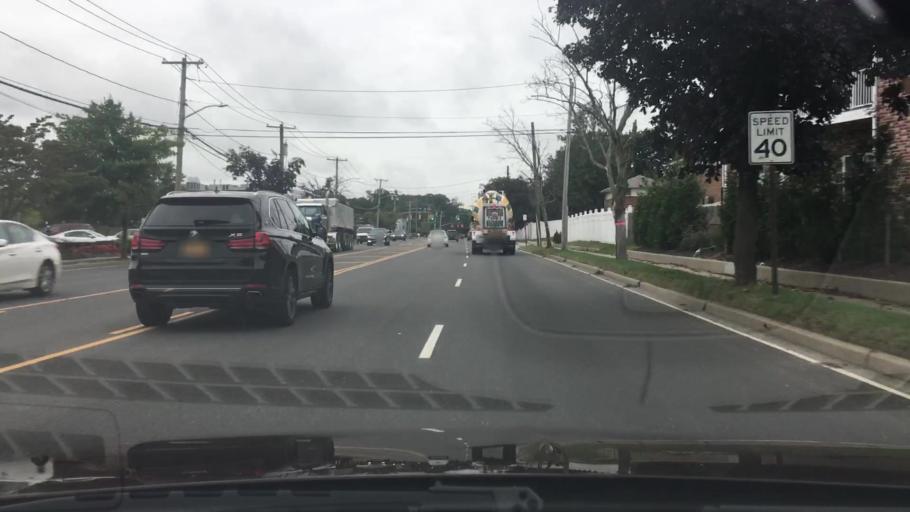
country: US
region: New York
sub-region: Nassau County
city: New Cassel
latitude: 40.7754
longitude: -73.5606
